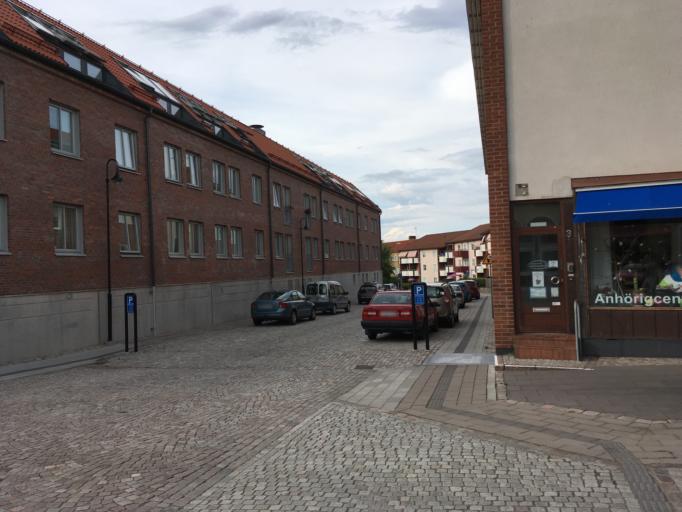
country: SE
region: Halland
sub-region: Laholms Kommun
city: Laholm
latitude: 56.5129
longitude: 13.0451
